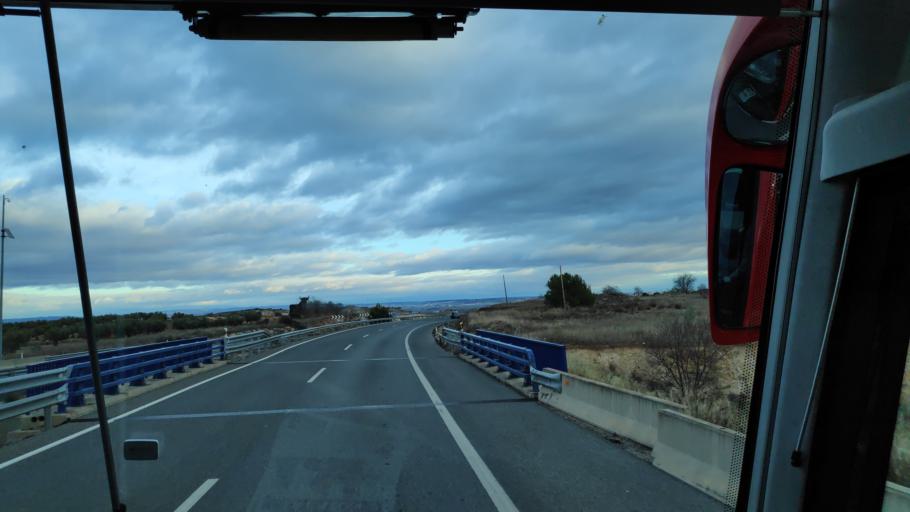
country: ES
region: Madrid
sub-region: Provincia de Madrid
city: Villarejo de Salvanes
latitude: 40.1509
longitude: -3.2359
